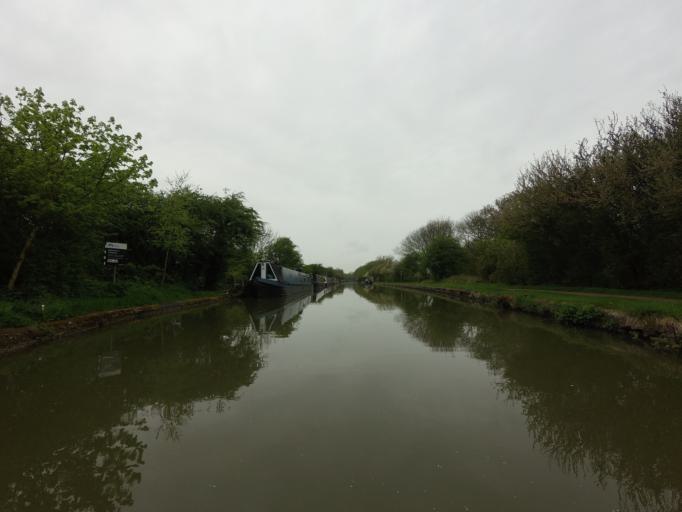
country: GB
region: England
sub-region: Milton Keynes
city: Stony Stratford
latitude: 52.0689
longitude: -0.8340
